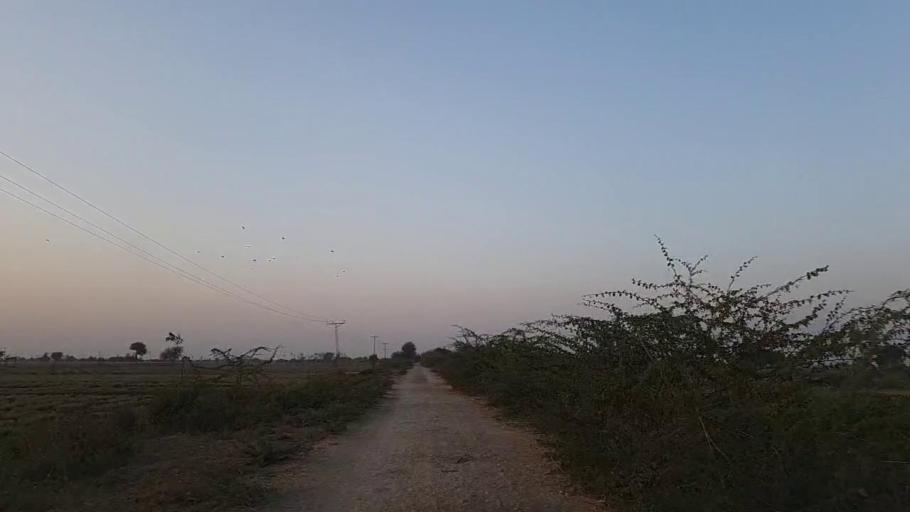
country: PK
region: Sindh
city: Naukot
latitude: 24.8820
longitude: 69.3716
